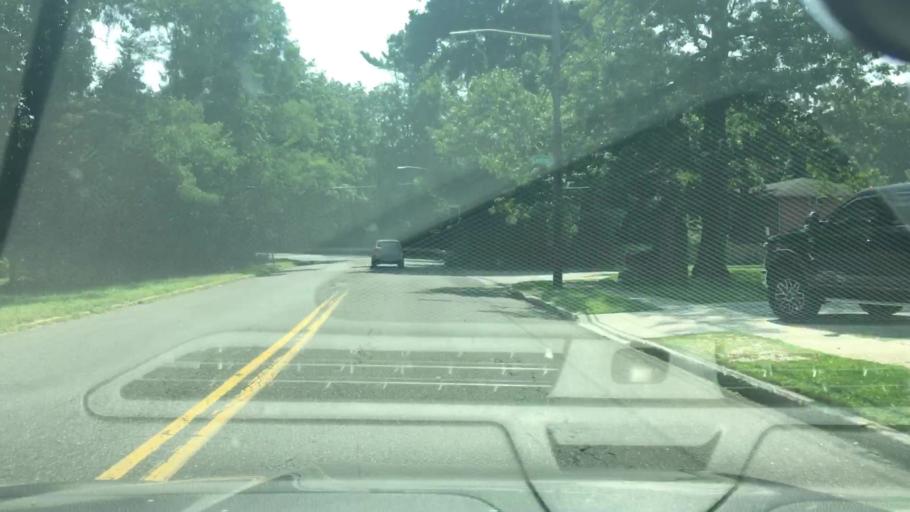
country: US
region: New York
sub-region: Suffolk County
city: Hauppauge
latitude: 40.8210
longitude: -73.2344
